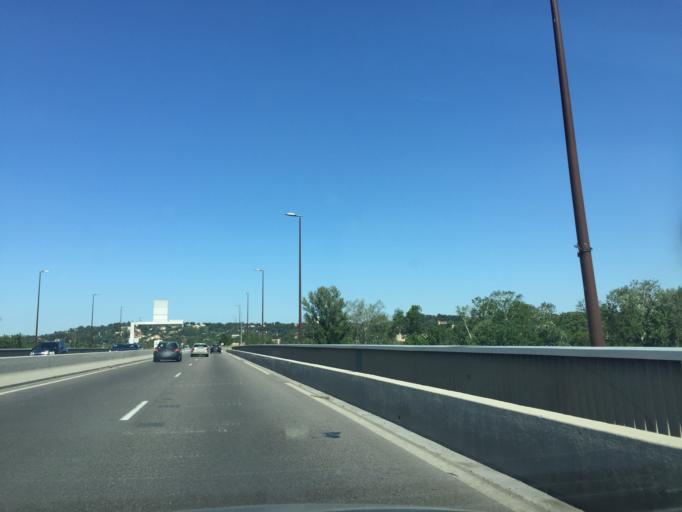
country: FR
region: Provence-Alpes-Cote d'Azur
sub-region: Departement du Vaucluse
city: Avignon
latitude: 43.9445
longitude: 4.7950
